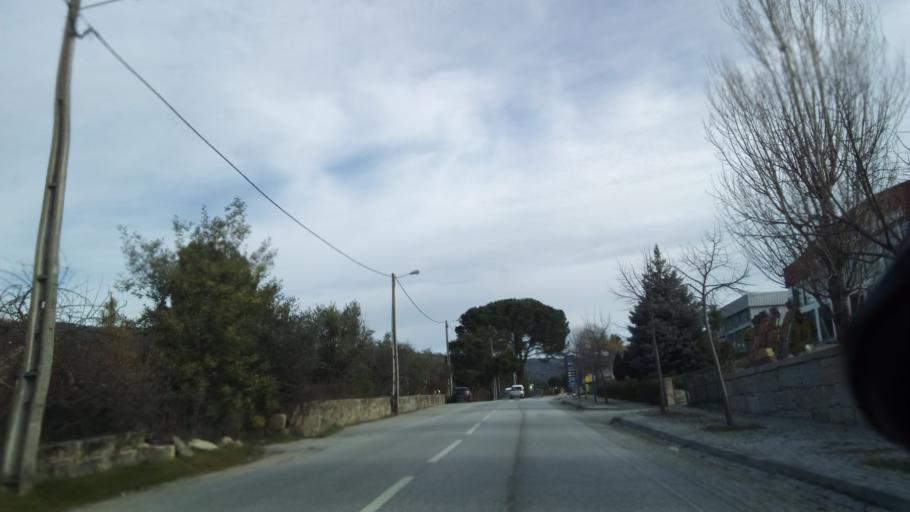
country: PT
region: Guarda
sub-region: Fornos de Algodres
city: Fornos de Algodres
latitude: 40.6118
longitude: -7.5336
